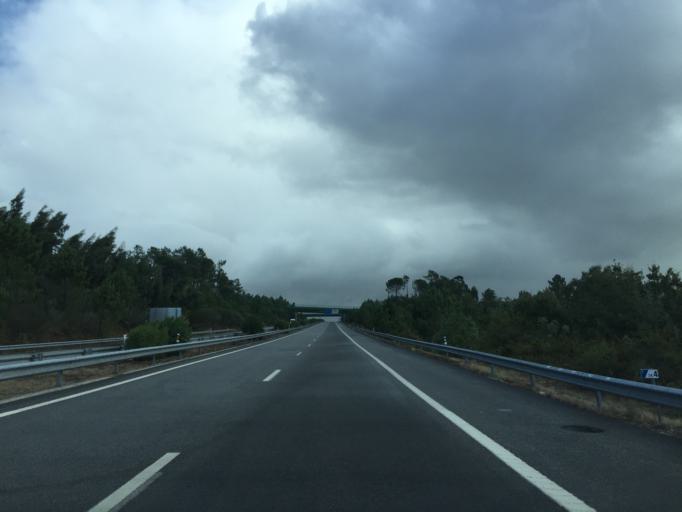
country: PT
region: Coimbra
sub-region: Cantanhede
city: Cantanhede
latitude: 40.2843
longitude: -8.5362
